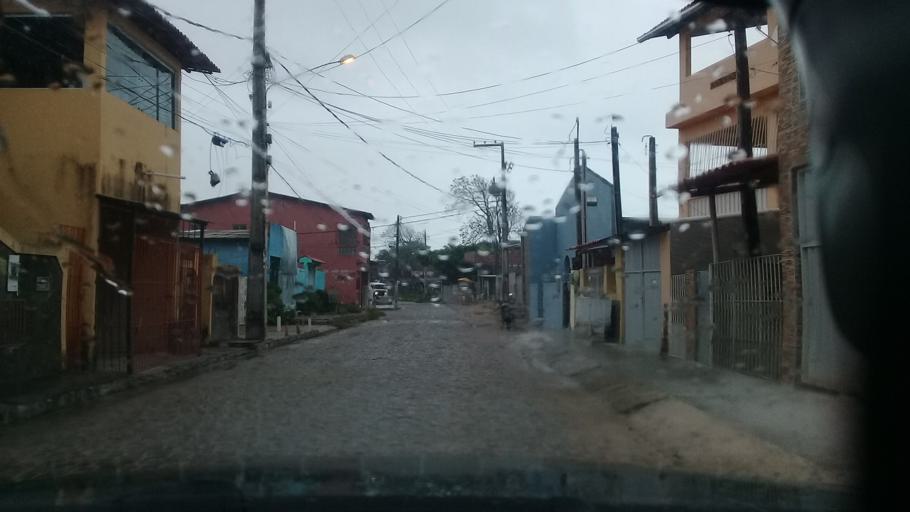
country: BR
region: Pernambuco
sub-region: Itamaraca
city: Itamaraca
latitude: -7.7450
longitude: -34.8273
